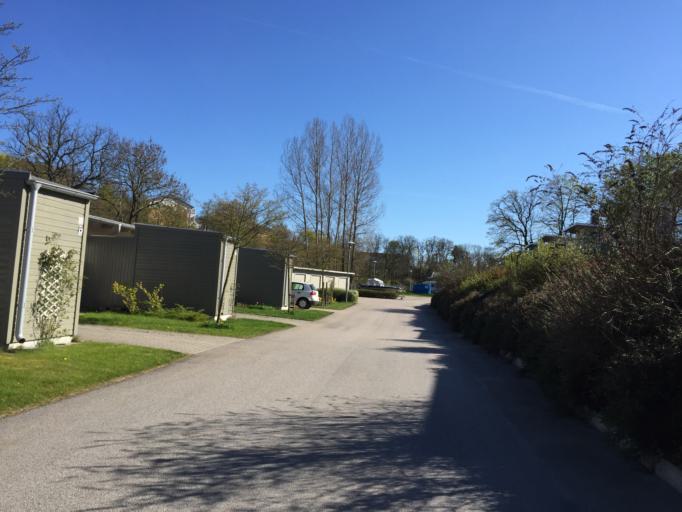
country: SE
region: Blekinge
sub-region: Karlskrona Kommun
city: Rodeby
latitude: 56.2000
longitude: 15.6628
